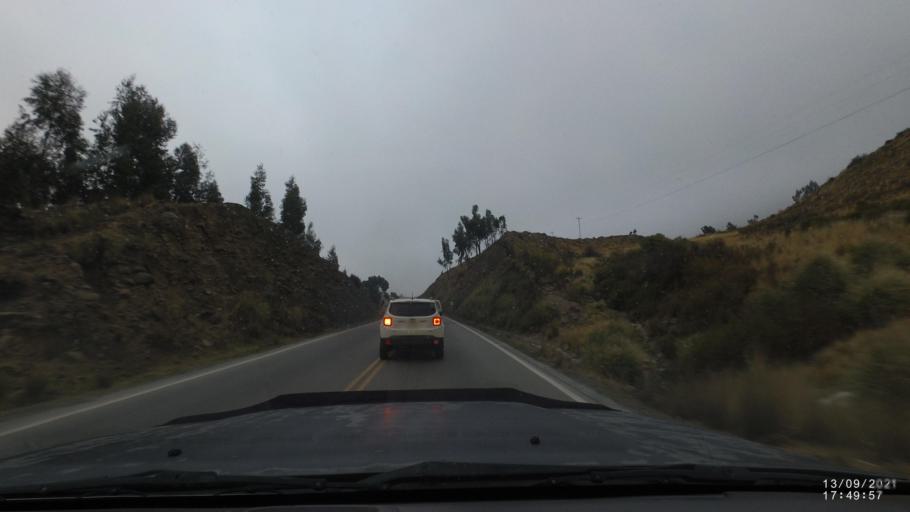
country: BO
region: Cochabamba
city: Colomi
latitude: -17.3942
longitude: -65.8563
